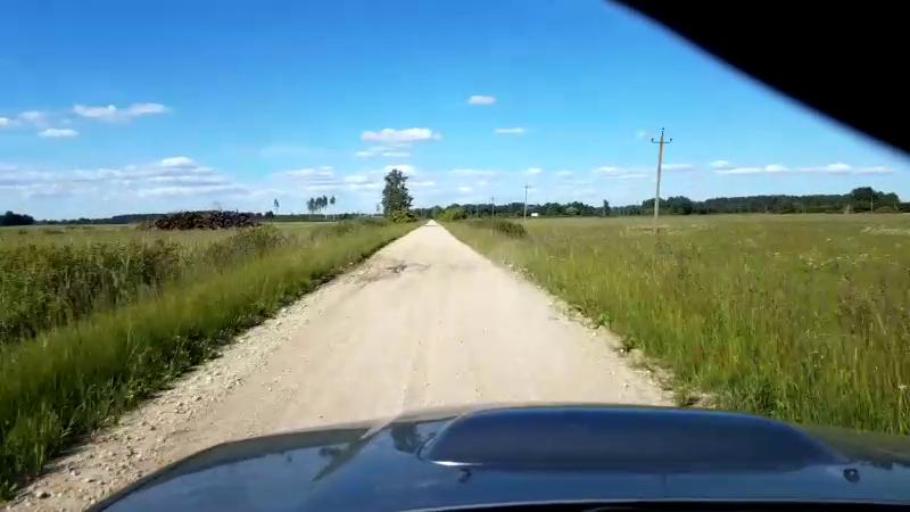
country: EE
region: Paernumaa
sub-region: Sauga vald
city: Sauga
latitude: 58.4959
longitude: 24.5577
